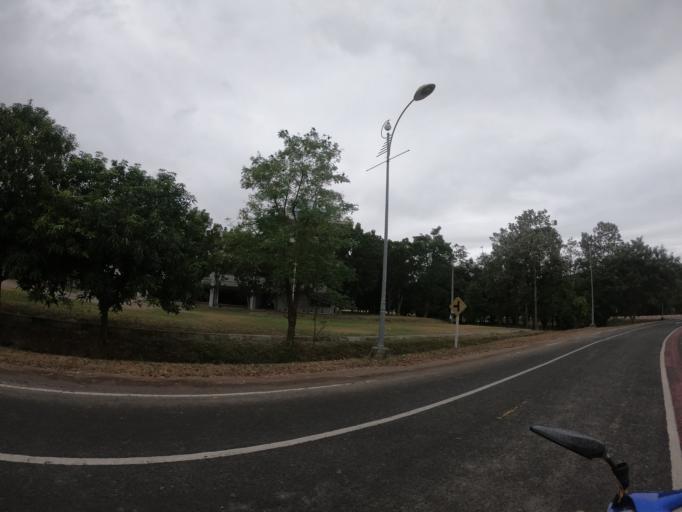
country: TH
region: Roi Et
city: Chiang Khwan
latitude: 16.1426
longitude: 103.8790
